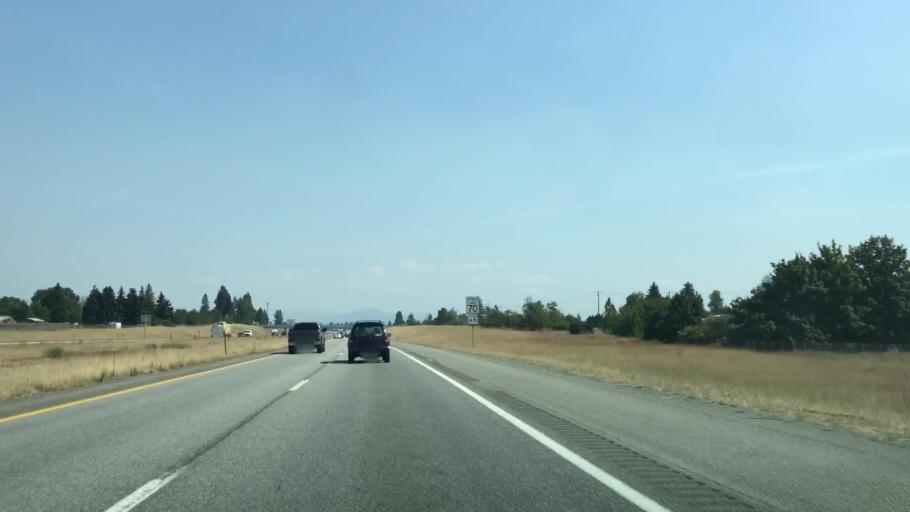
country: US
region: Idaho
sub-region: Kootenai County
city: Post Falls
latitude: 47.7110
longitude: -116.9899
